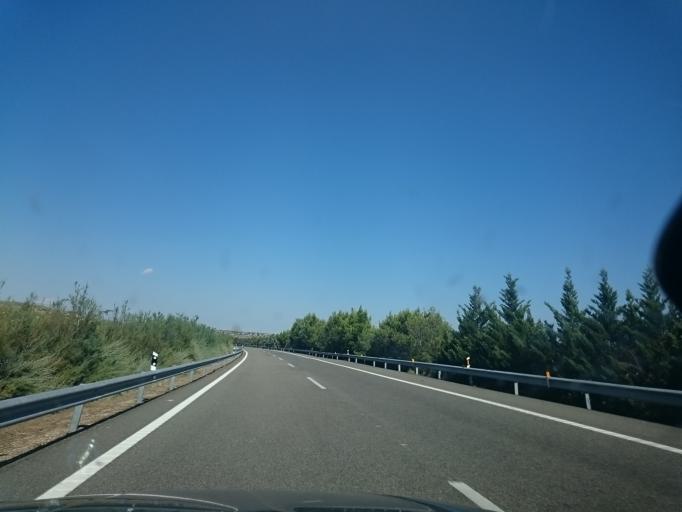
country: ES
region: Aragon
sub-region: Provincia de Huesca
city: Penalba
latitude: 41.5125
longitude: -0.0671
